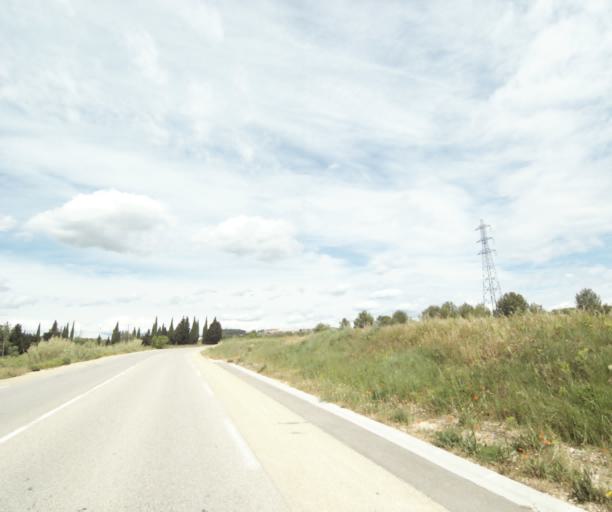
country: FR
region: Provence-Alpes-Cote d'Azur
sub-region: Departement des Bouches-du-Rhone
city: Rognac
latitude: 43.5092
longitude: 5.2401
